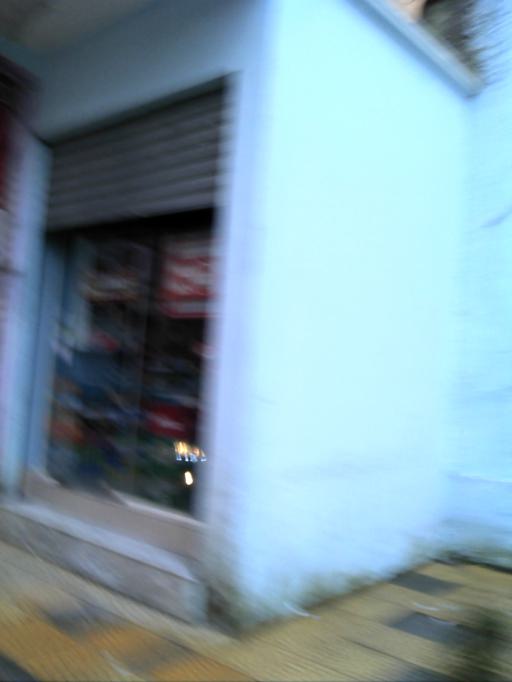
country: AL
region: Shkoder
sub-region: Rrethi i Shkodres
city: Shkoder
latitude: 42.0688
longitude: 19.5141
